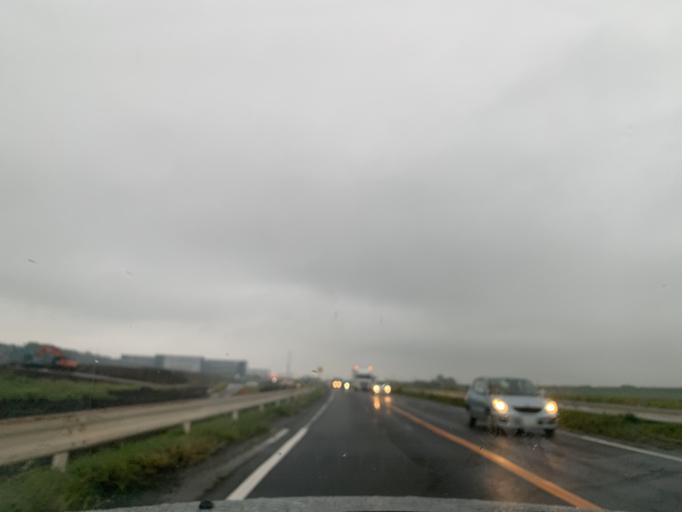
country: JP
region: Chiba
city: Nagareyama
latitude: 35.8947
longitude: 139.8930
